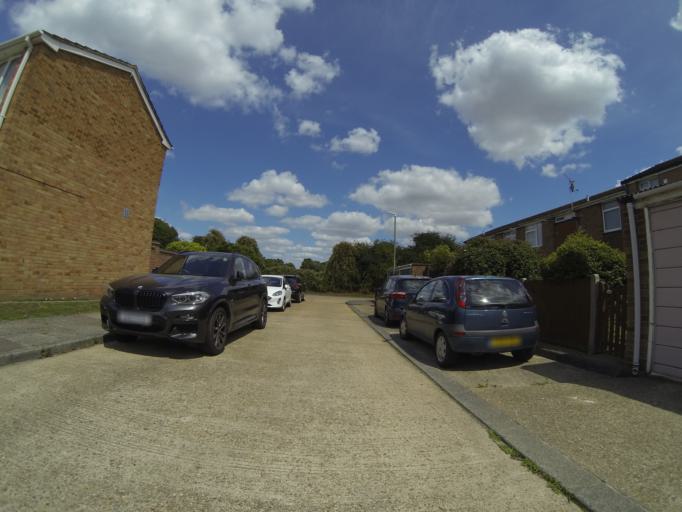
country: GB
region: England
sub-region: Greater London
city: Bexley
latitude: 51.4302
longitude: 0.1719
